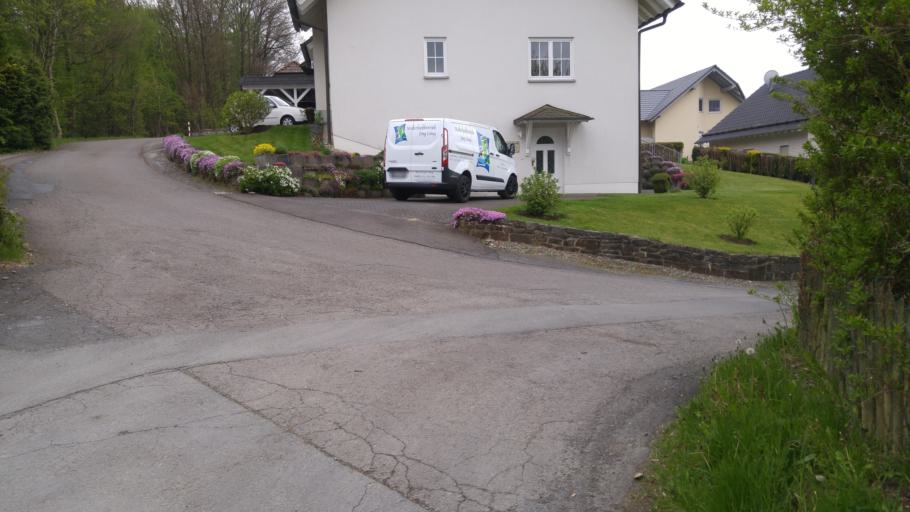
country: DE
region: North Rhine-Westphalia
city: Waldbrol
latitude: 50.9126
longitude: 7.6569
